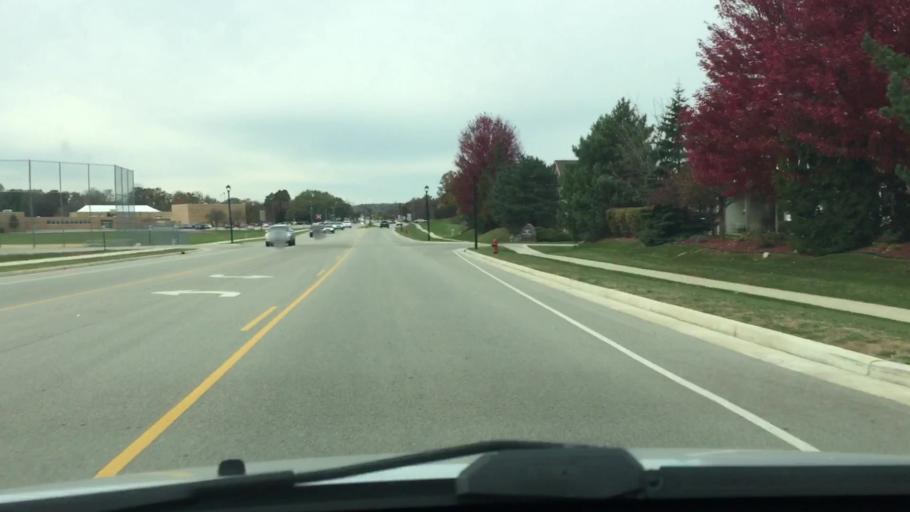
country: US
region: Wisconsin
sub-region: Waukesha County
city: Mukwonago
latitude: 42.8739
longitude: -88.3313
